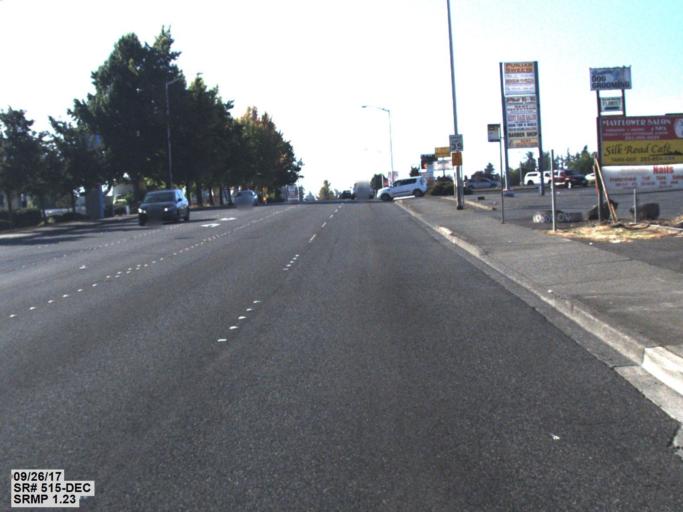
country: US
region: Washington
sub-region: King County
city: Kent
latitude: 47.3903
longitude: -122.2022
